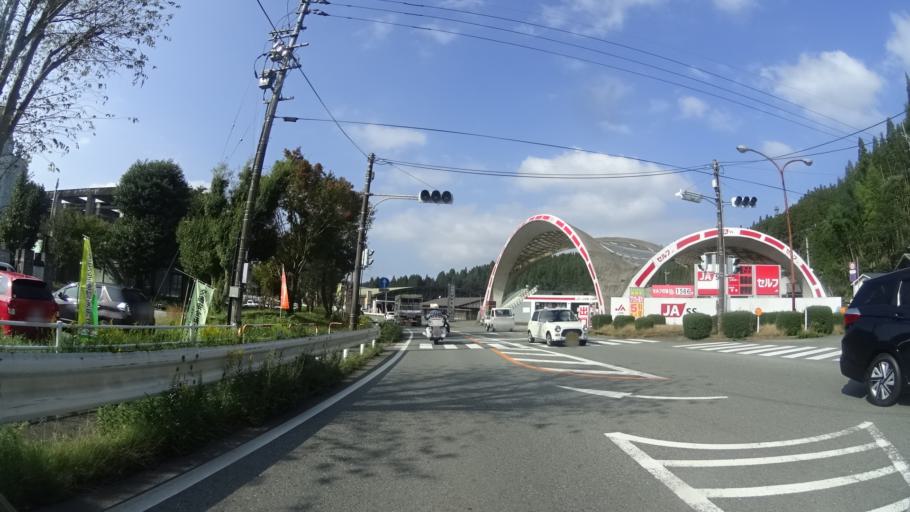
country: JP
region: Kumamoto
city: Aso
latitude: 33.1102
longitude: 131.0637
